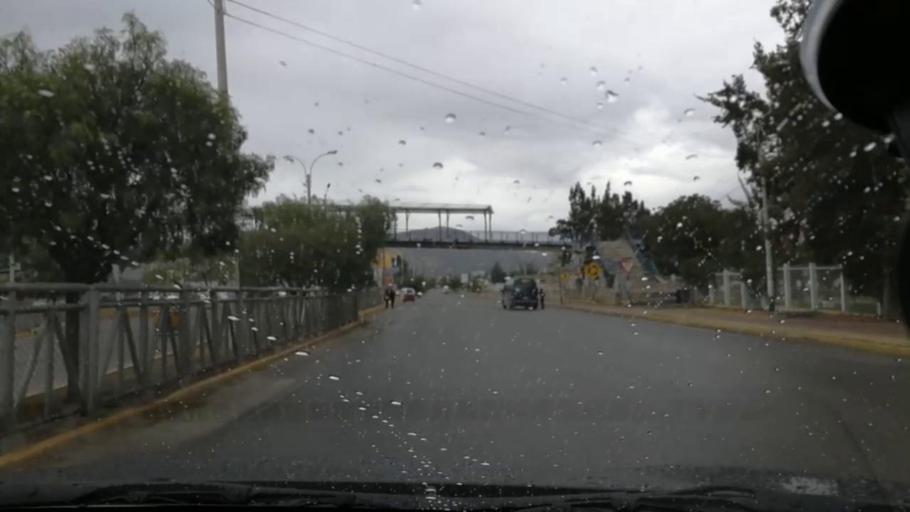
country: PE
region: Cajamarca
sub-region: Provincia de Cajamarca
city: Cajamarca
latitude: -7.1655
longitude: -78.4958
